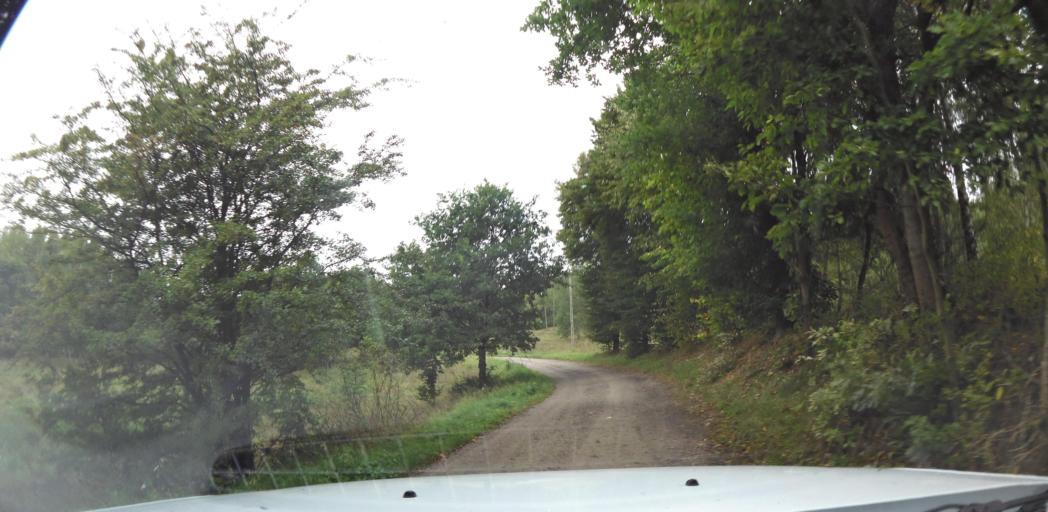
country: PL
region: West Pomeranian Voivodeship
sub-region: Powiat lobeski
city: Wegorzyno
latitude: 53.5204
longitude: 15.5971
